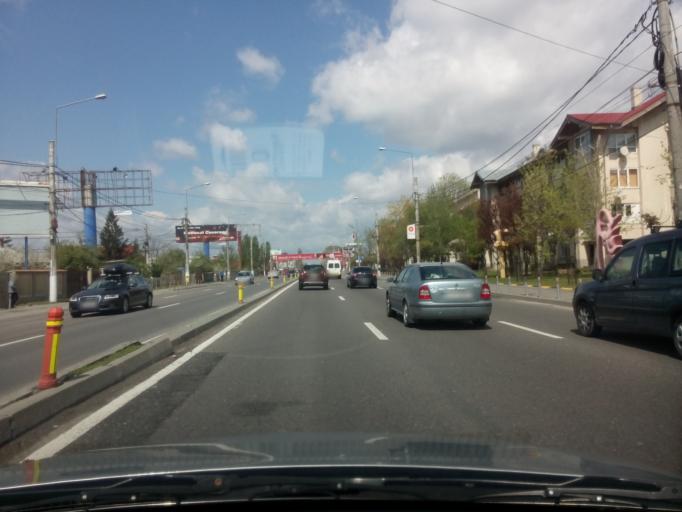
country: RO
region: Ilfov
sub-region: Comuna Otopeni
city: Otopeni
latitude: 44.5522
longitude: 26.0691
